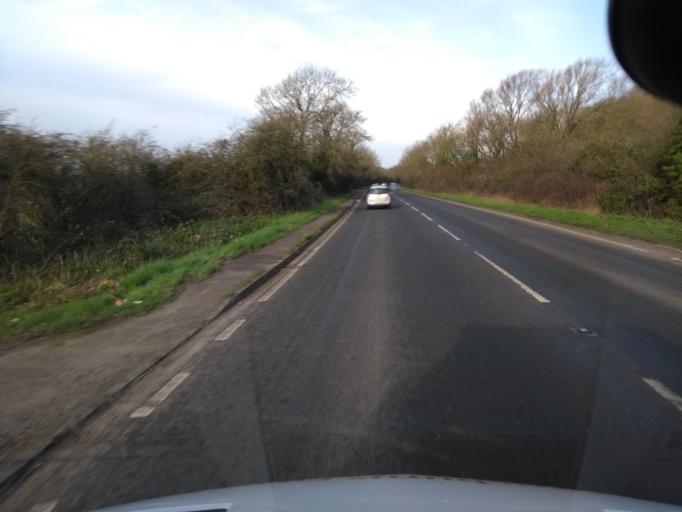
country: GB
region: England
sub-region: North Somerset
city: Bleadon
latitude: 51.3116
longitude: -2.9636
